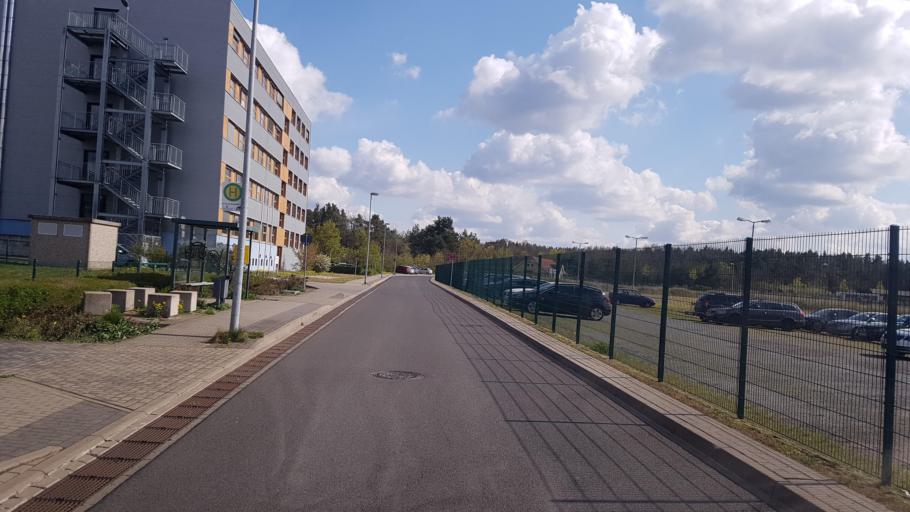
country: DE
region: Brandenburg
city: Luckenwalde
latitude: 52.0777
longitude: 13.1546
